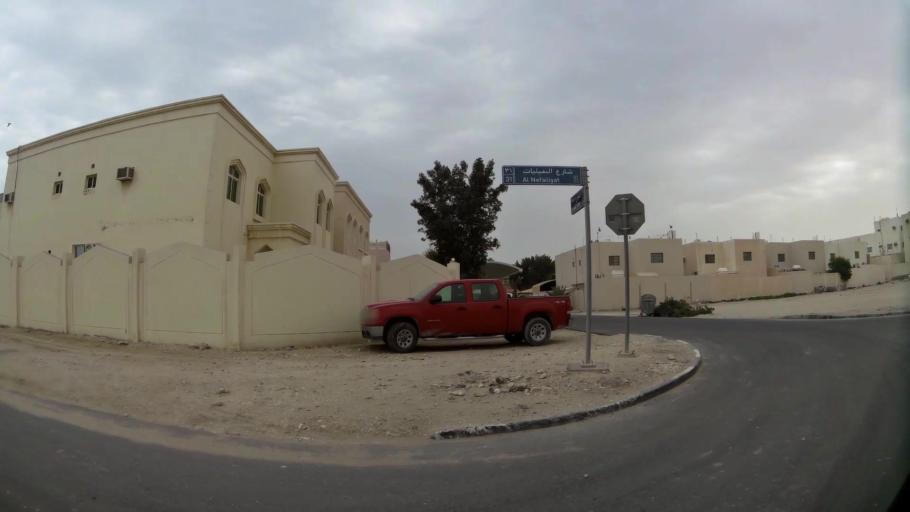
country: QA
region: Baladiyat ar Rayyan
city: Ar Rayyan
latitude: 25.3454
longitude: 51.4648
